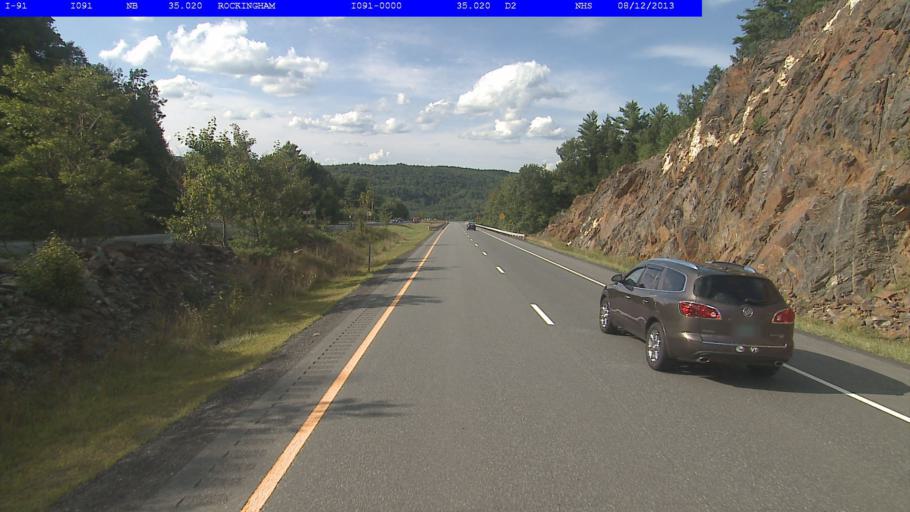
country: US
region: Vermont
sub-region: Windham County
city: Rockingham
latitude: 43.1761
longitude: -72.4628
